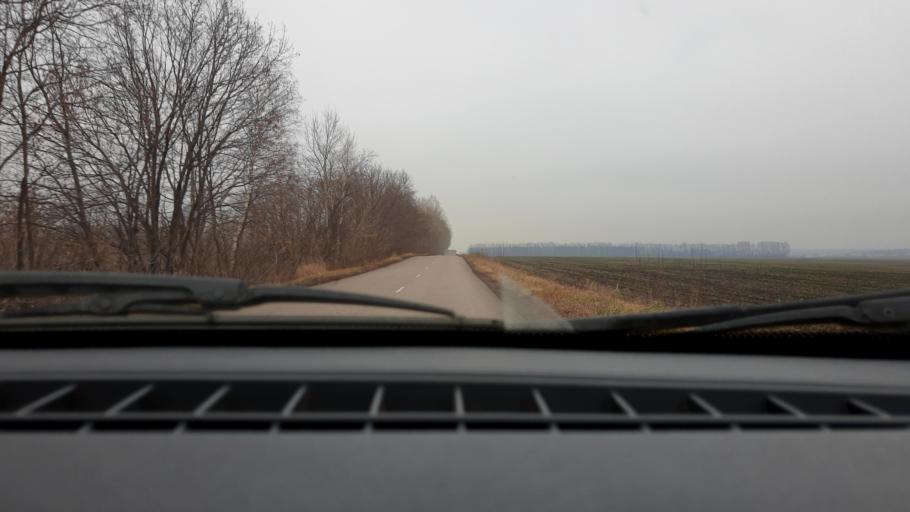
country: RU
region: Bashkortostan
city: Mikhaylovka
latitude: 54.8514
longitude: 55.7853
